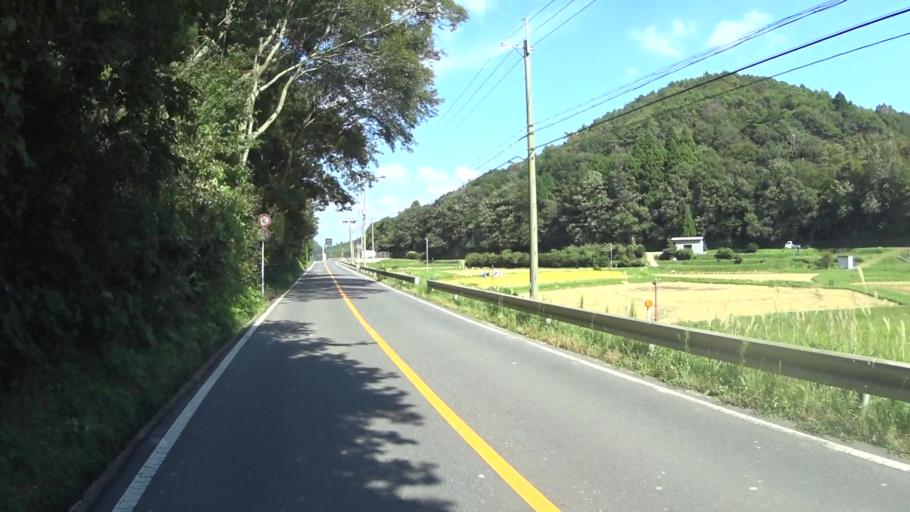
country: JP
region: Kyoto
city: Kameoka
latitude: 34.9734
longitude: 135.5180
